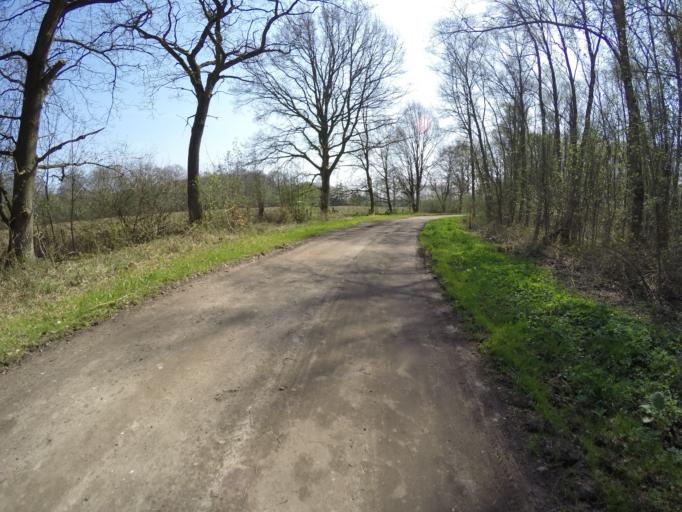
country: DE
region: Schleswig-Holstein
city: Hemdingen
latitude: 53.7327
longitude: 9.8276
